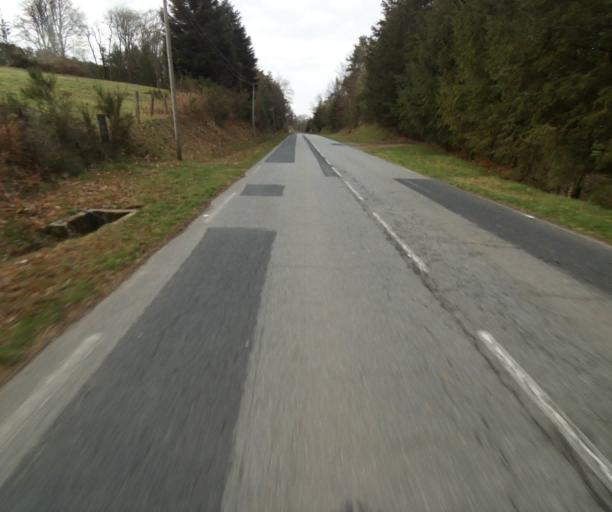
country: FR
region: Limousin
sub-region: Departement de la Correze
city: Correze
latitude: 45.3895
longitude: 1.8639
